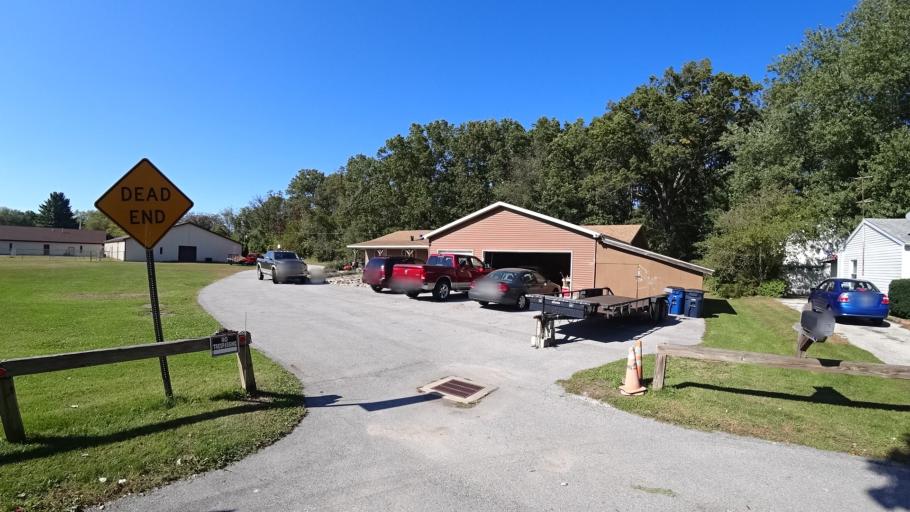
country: US
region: Indiana
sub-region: LaPorte County
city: Michigan City
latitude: 41.6926
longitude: -86.9008
